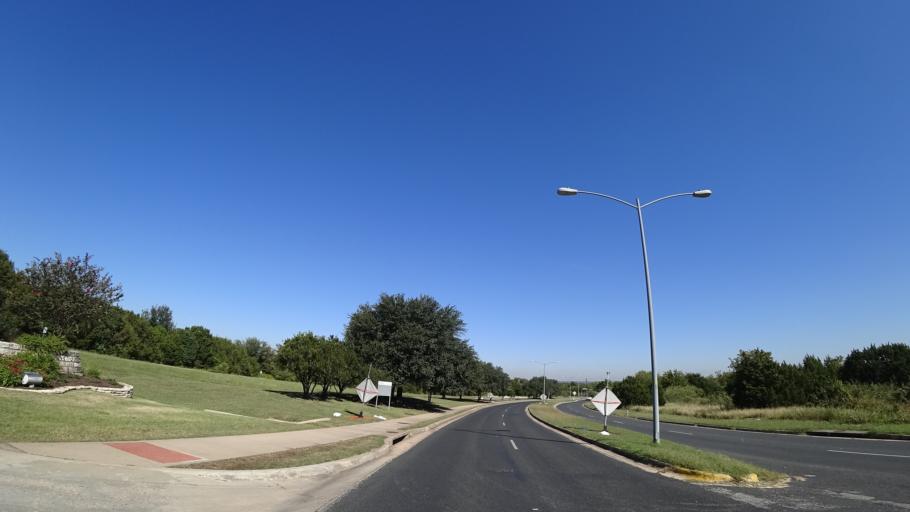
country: US
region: Texas
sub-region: Travis County
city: Austin
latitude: 30.2248
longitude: -97.7088
